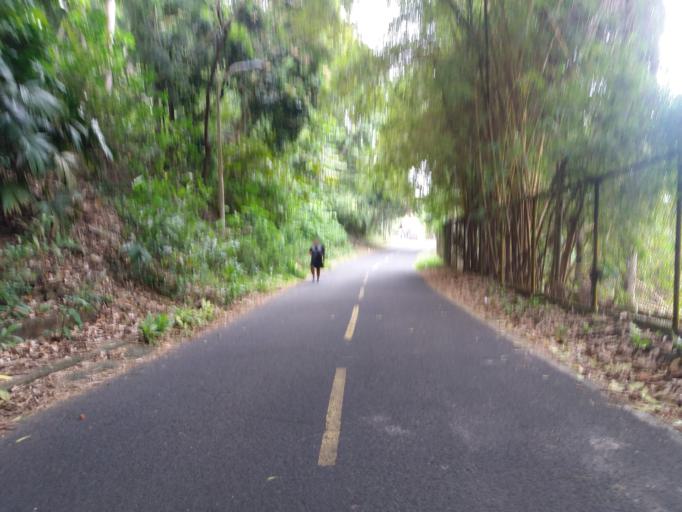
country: PA
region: Panama
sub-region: Distrito de Panama
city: Ancon
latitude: 8.9531
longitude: -79.5491
